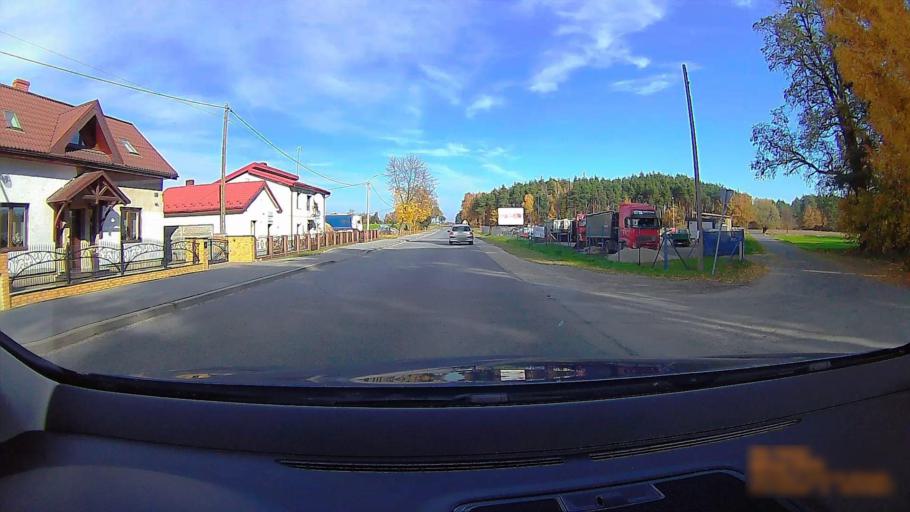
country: PL
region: Greater Poland Voivodeship
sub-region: Powiat ostrzeszowski
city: Doruchow
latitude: 51.3692
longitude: 18.0332
